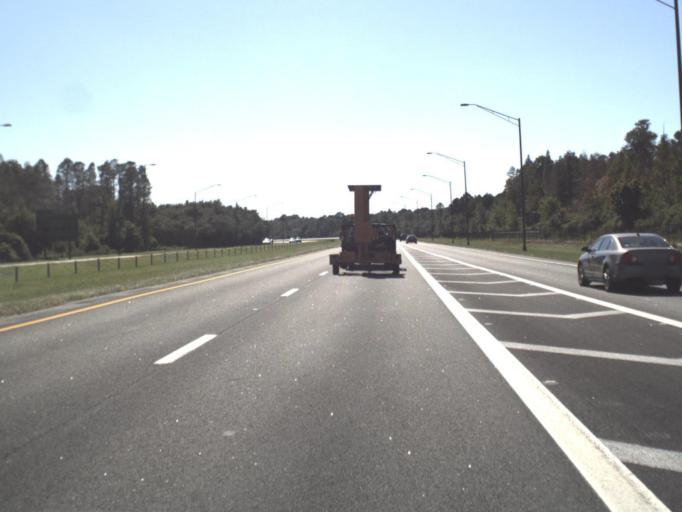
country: US
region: Florida
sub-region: Pasco County
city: Shady Hills
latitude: 28.3263
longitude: -82.5531
